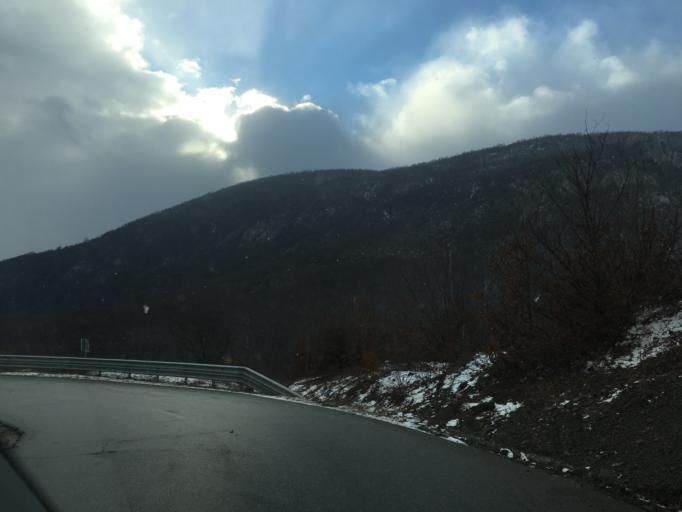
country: XK
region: Pec
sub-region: Komuna e Pejes
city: Dubova (Driloni)
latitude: 42.7498
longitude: 20.3032
